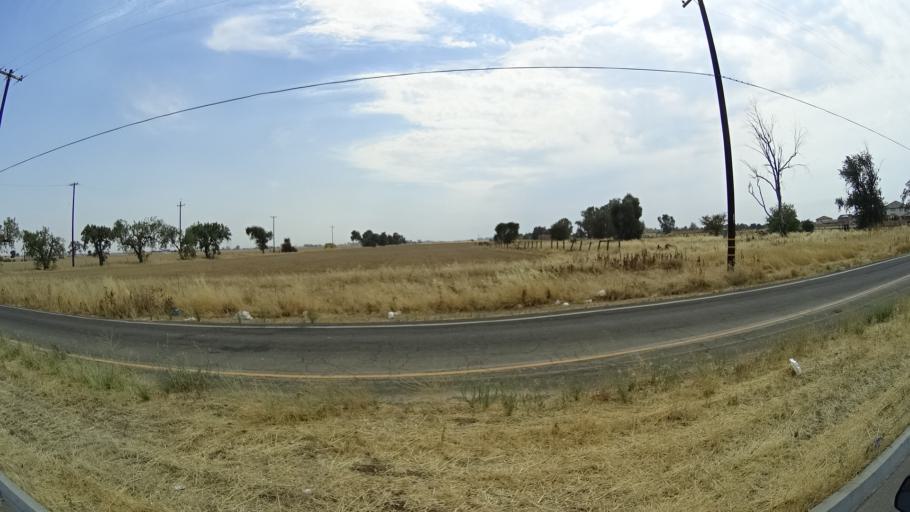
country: US
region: California
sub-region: Sacramento County
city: Laguna
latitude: 38.3908
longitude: -121.4091
